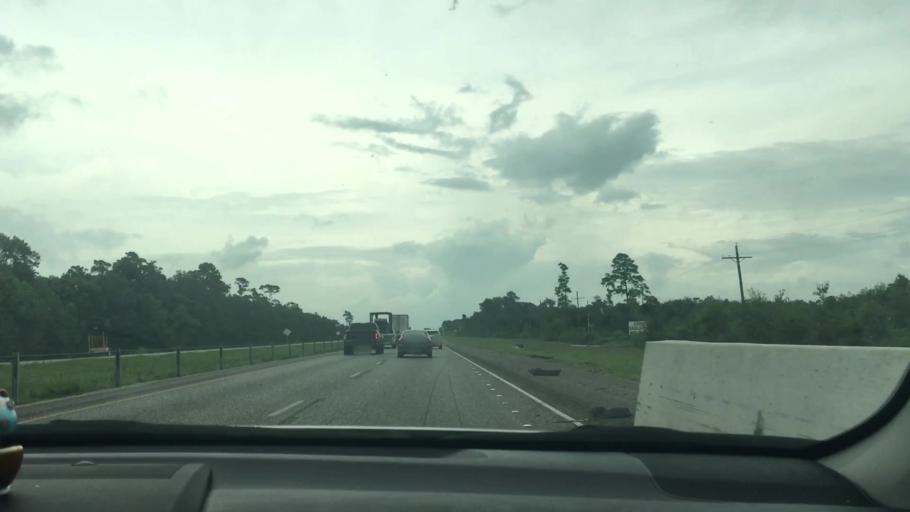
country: US
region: Texas
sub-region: Jefferson County
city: Fannett
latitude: 29.9244
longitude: -94.2778
